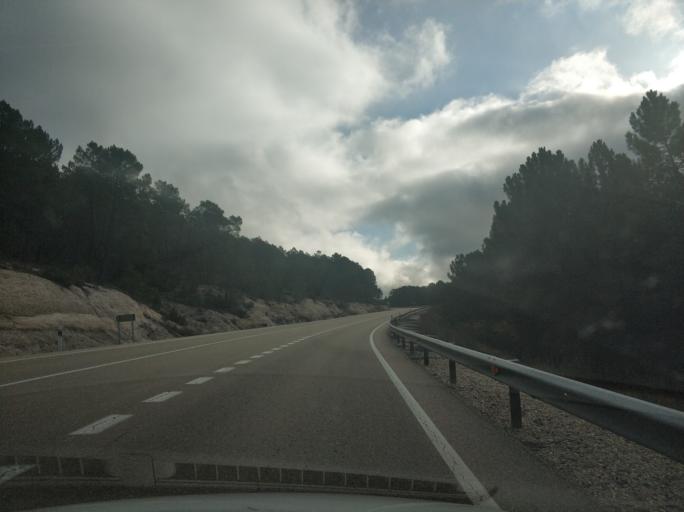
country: ES
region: Castille and Leon
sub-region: Provincia de Soria
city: Navaleno
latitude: 41.8322
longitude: -2.9852
